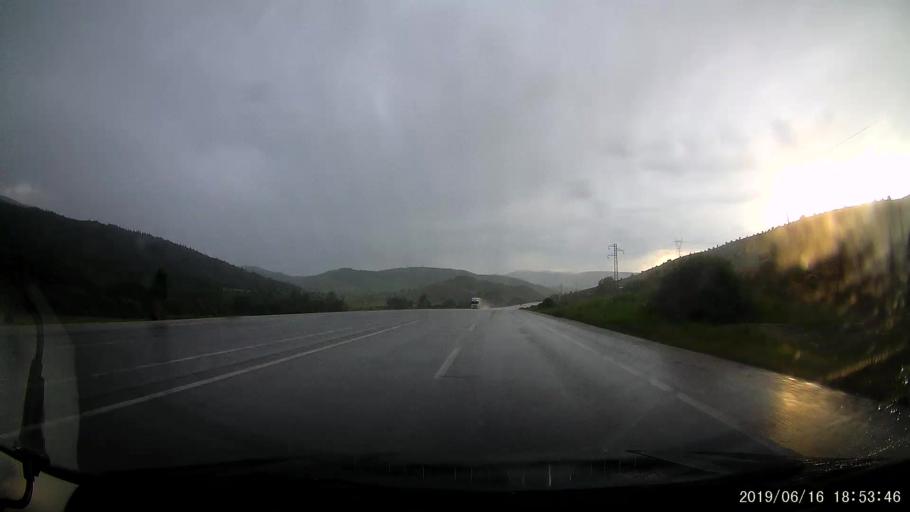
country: TR
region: Erzincan
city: Catalcam
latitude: 39.8971
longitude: 38.8693
